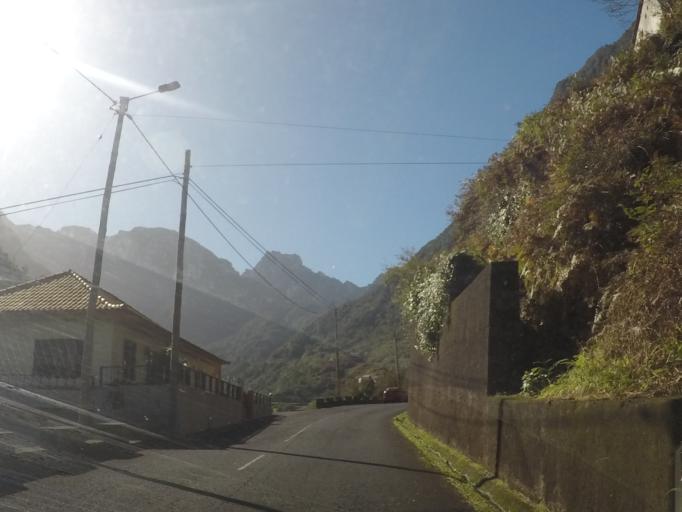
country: PT
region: Madeira
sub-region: Sao Vicente
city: Sao Vicente
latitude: 32.7952
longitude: -16.9711
